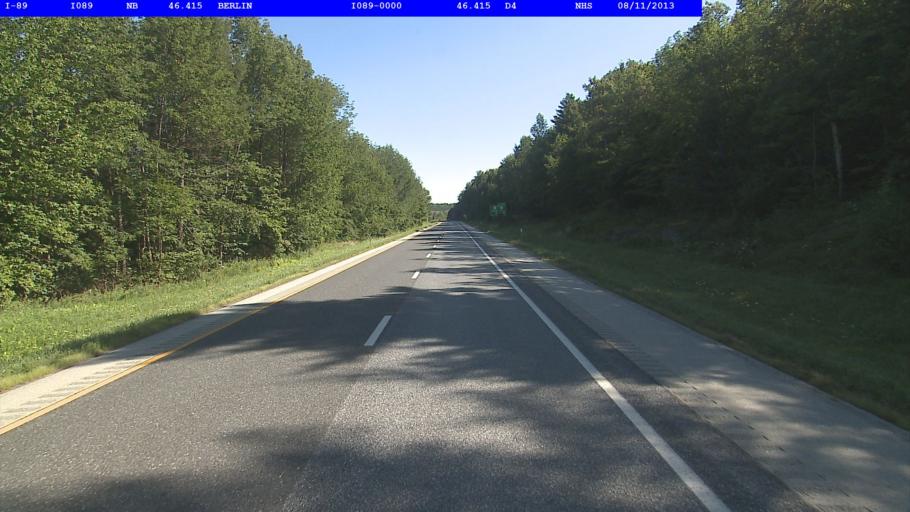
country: US
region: Vermont
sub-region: Orange County
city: Williamstown
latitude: 44.1612
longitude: -72.5817
